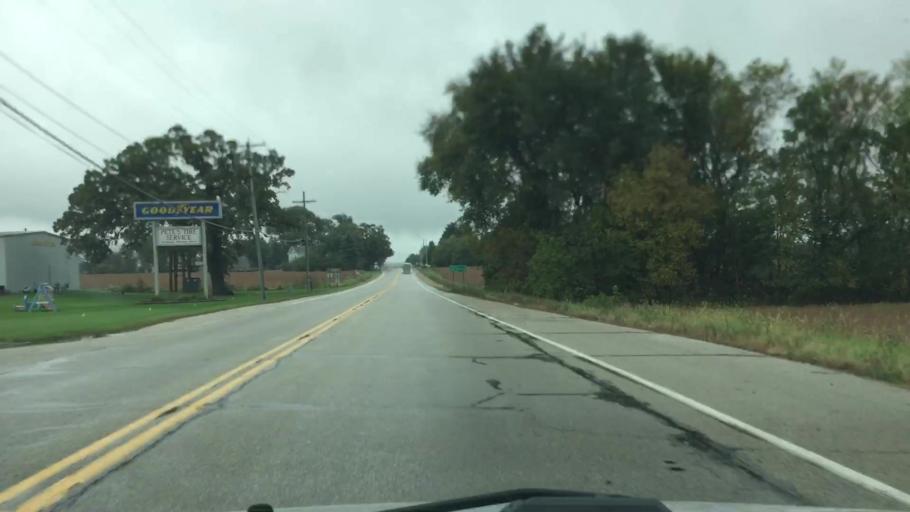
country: US
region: Wisconsin
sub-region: Walworth County
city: Whitewater
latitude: 42.8287
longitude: -88.7082
